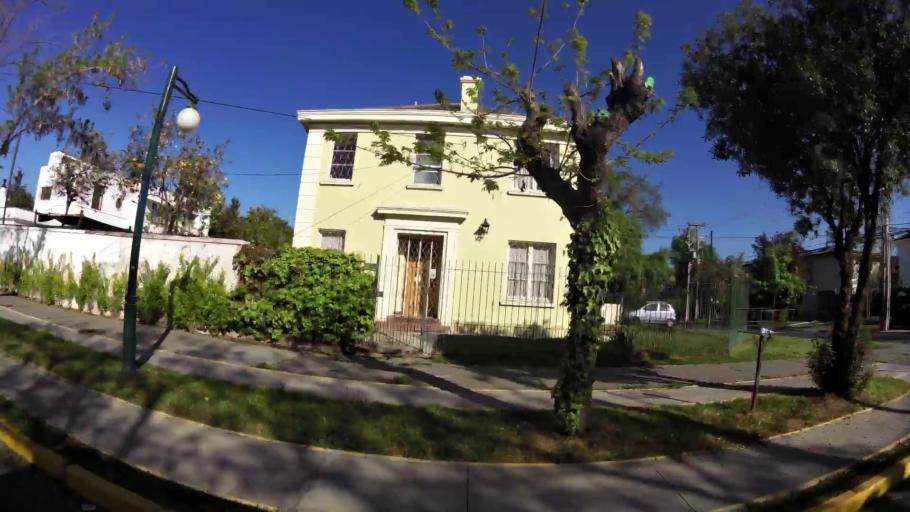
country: CL
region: Santiago Metropolitan
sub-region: Provincia de Santiago
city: Villa Presidente Frei, Nunoa, Santiago, Chile
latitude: -33.4449
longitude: -70.5846
